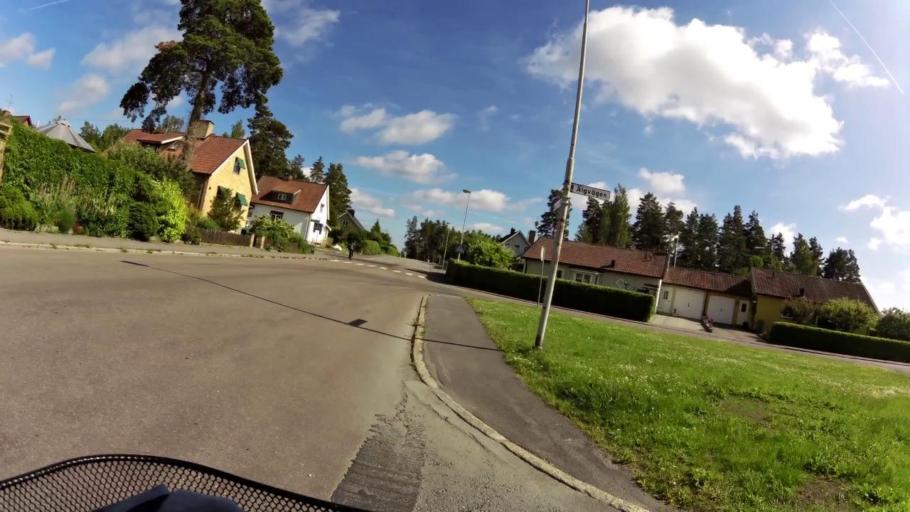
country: SE
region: OEstergoetland
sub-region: Linkopings Kommun
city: Linkoping
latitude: 58.3905
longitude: 15.6578
